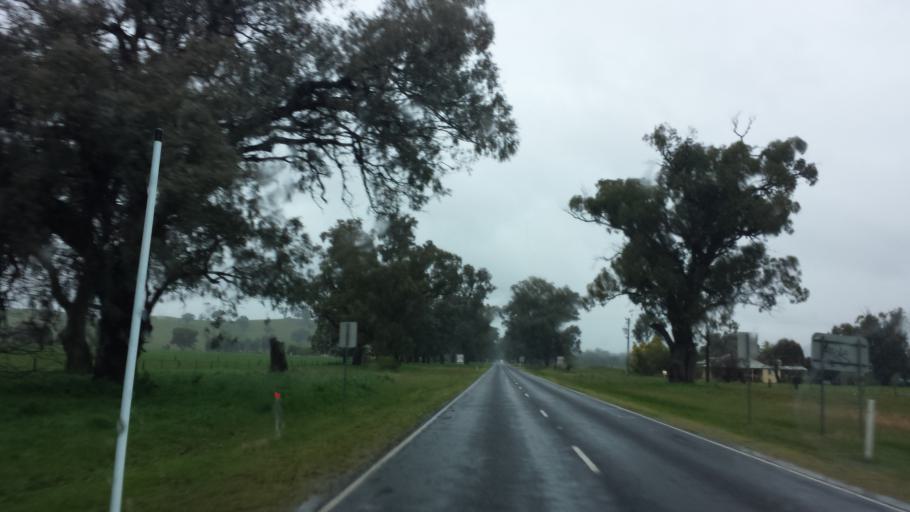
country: AU
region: Victoria
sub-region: Wangaratta
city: Wangaratta
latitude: -36.4380
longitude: 146.5456
